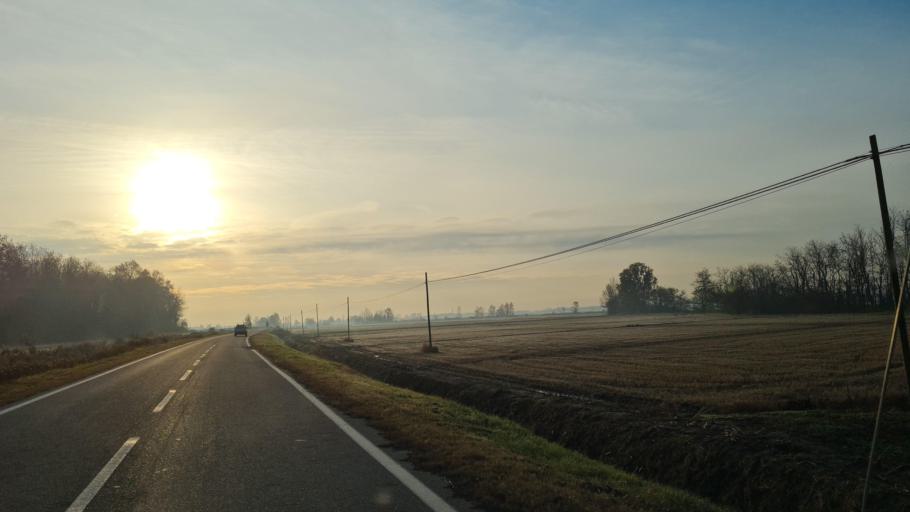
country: IT
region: Piedmont
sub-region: Provincia di Vercelli
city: Villarboit
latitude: 45.4448
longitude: 8.3195
